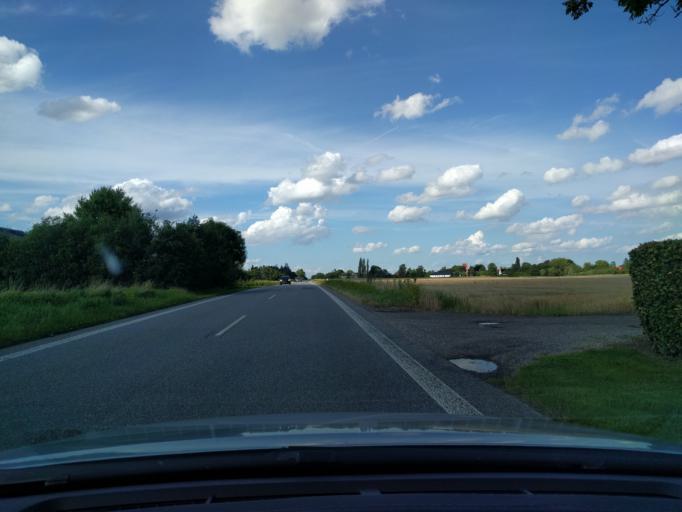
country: DK
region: Zealand
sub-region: Guldborgsund Kommune
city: Stubbekobing
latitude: 54.8293
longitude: 11.9953
